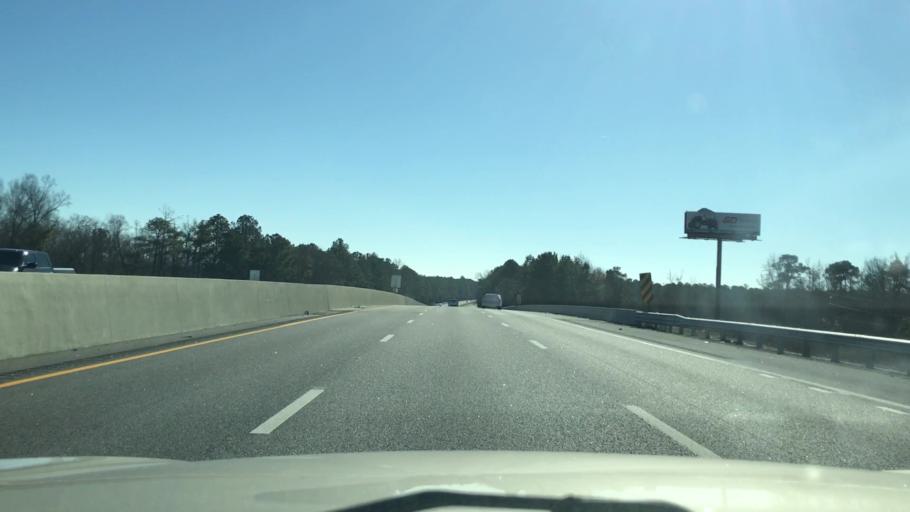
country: US
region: South Carolina
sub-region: Lexington County
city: Pineridge
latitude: 33.9166
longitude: -81.0623
